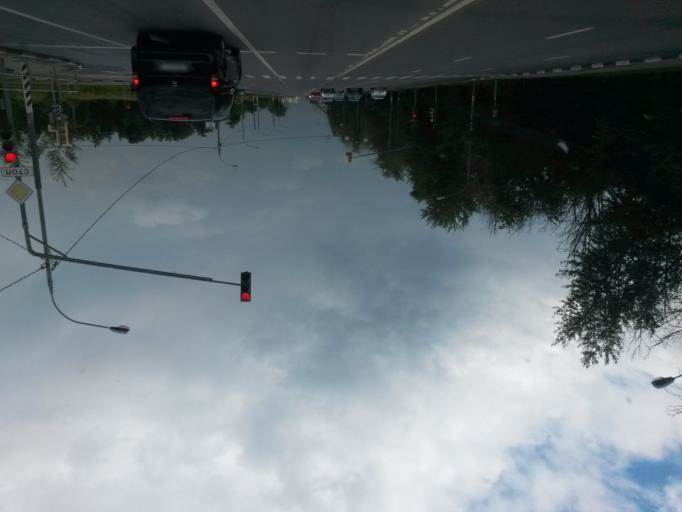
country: RU
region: Moskovskaya
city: Shcherbinka
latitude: 55.5066
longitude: 37.5740
